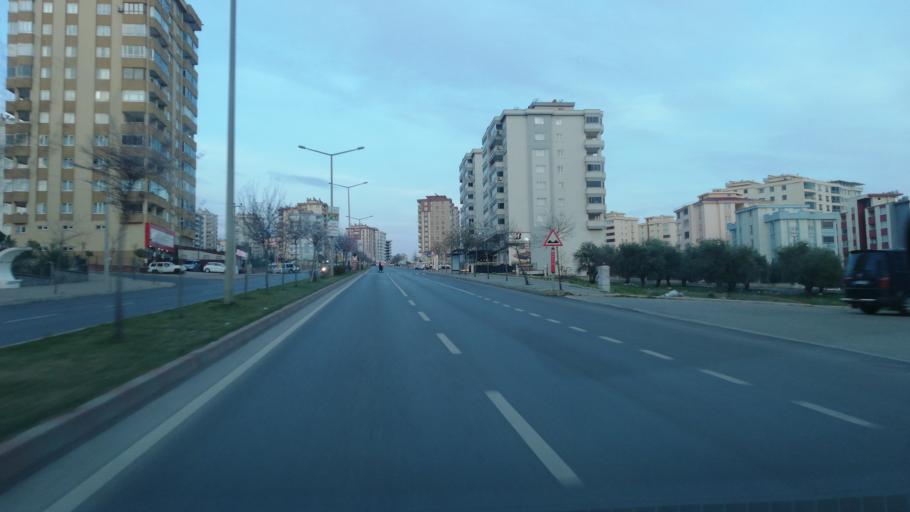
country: TR
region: Kahramanmaras
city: Kahramanmaras
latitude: 37.5831
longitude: 36.8735
